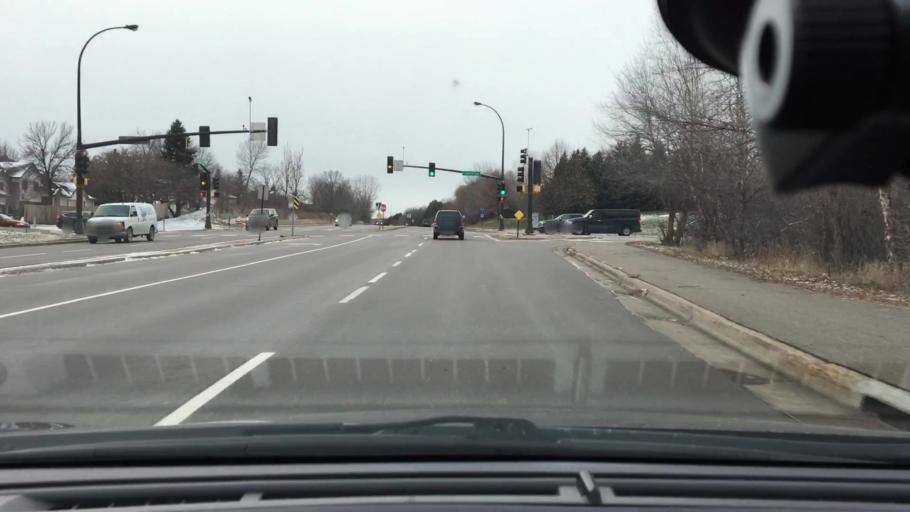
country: US
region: Minnesota
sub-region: Hennepin County
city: Plymouth
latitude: 45.0328
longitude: -93.4336
